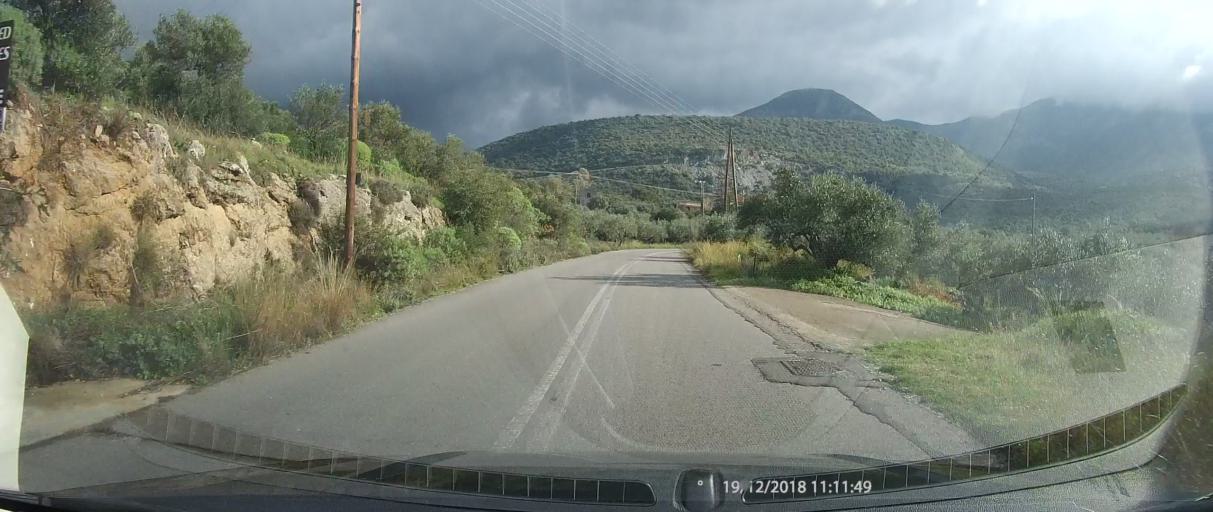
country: GR
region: Peloponnese
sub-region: Nomos Messinias
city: Kardamyli
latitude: 36.8190
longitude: 22.3033
